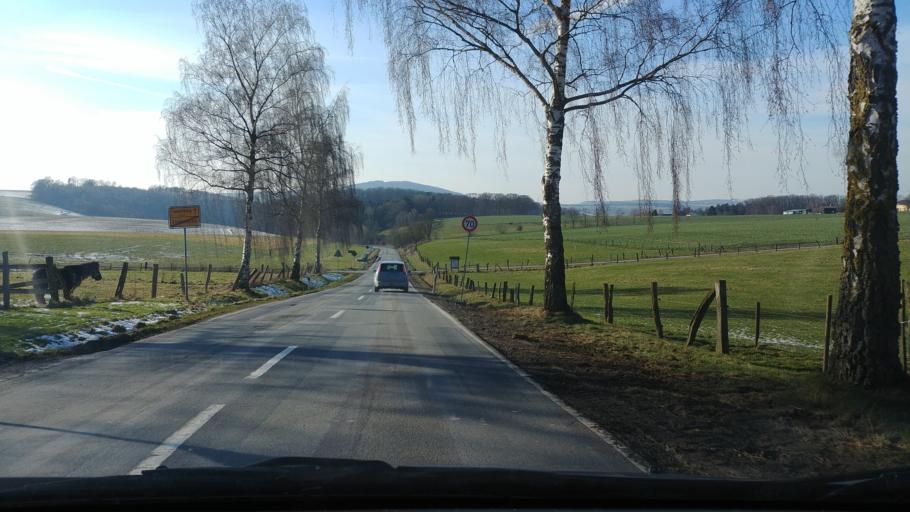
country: DE
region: Hesse
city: Trendelburg
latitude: 51.5741
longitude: 9.4584
